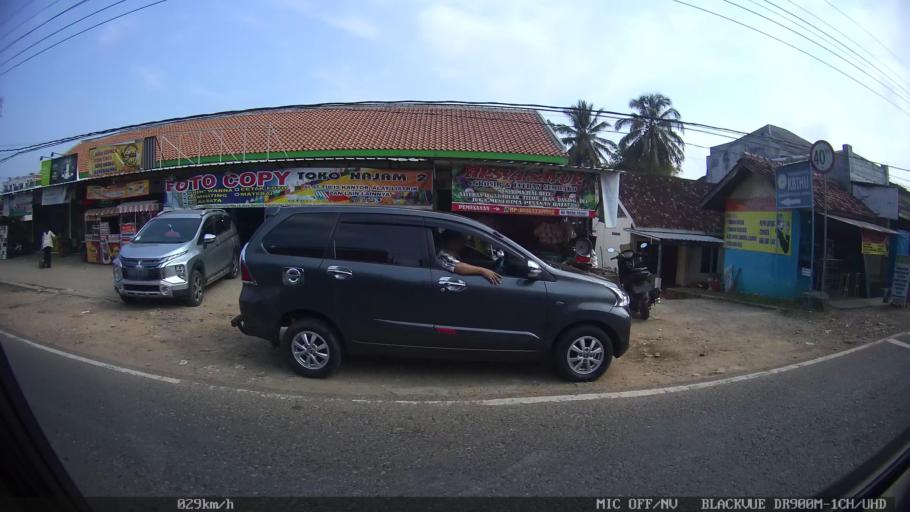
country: ID
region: Lampung
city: Natar
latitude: -5.3661
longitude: 105.1638
